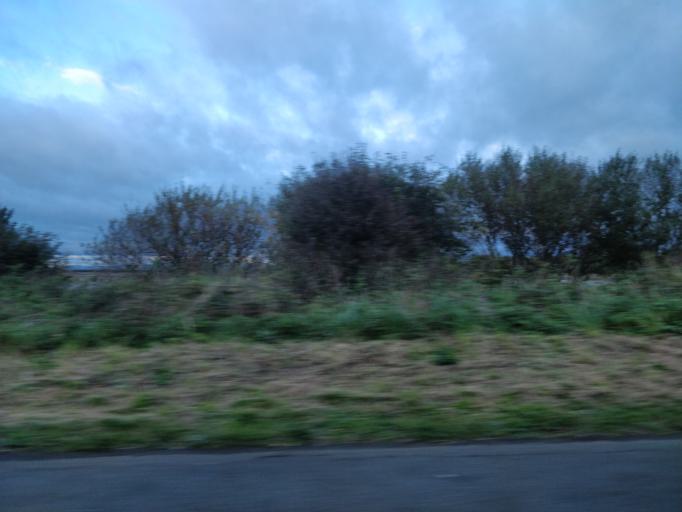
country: GB
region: England
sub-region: Sefton
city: Southport
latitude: 53.6661
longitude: -2.9916
